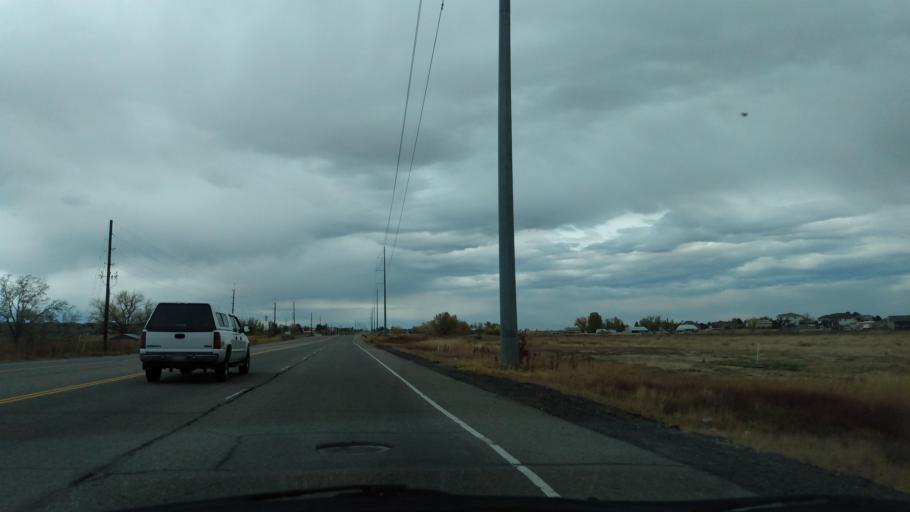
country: US
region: Colorado
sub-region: Adams County
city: Northglenn
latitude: 39.9441
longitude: -104.9781
